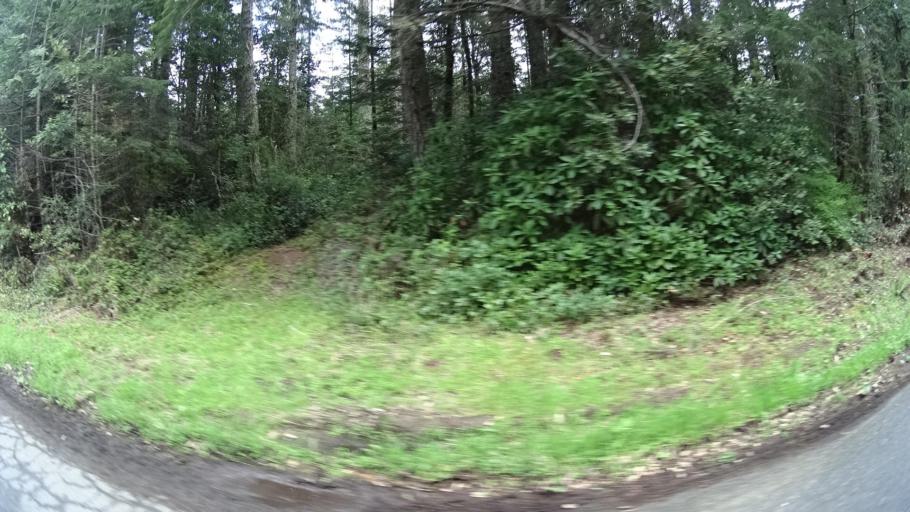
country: US
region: California
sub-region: Humboldt County
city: Blue Lake
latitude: 40.8040
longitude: -123.9874
